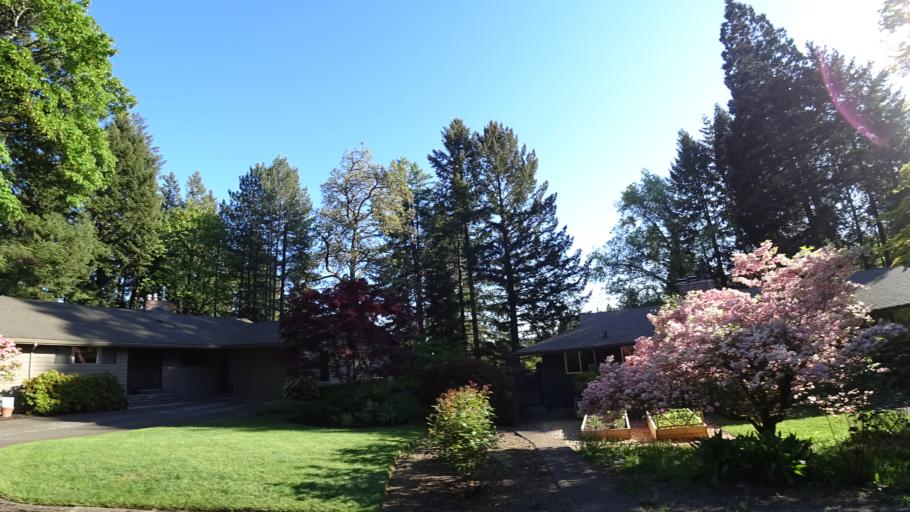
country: US
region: Oregon
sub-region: Washington County
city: West Slope
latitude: 45.5001
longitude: -122.7709
